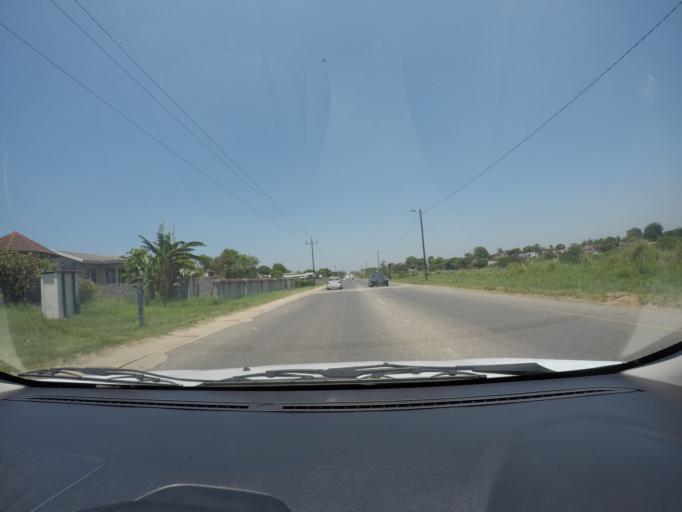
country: ZA
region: KwaZulu-Natal
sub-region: uThungulu District Municipality
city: eSikhawini
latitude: -28.8792
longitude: 31.9098
